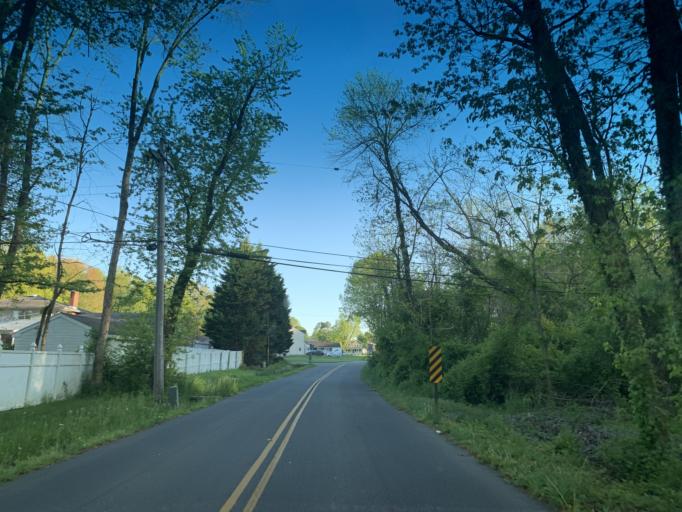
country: US
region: Maryland
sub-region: Harford County
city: Aberdeen
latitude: 39.5300
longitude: -76.1742
